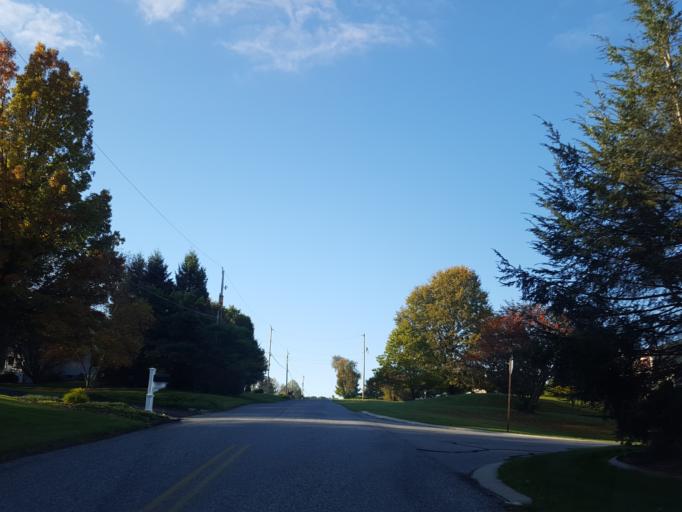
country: US
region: Pennsylvania
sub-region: York County
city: Yoe
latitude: 39.9405
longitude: -76.6325
